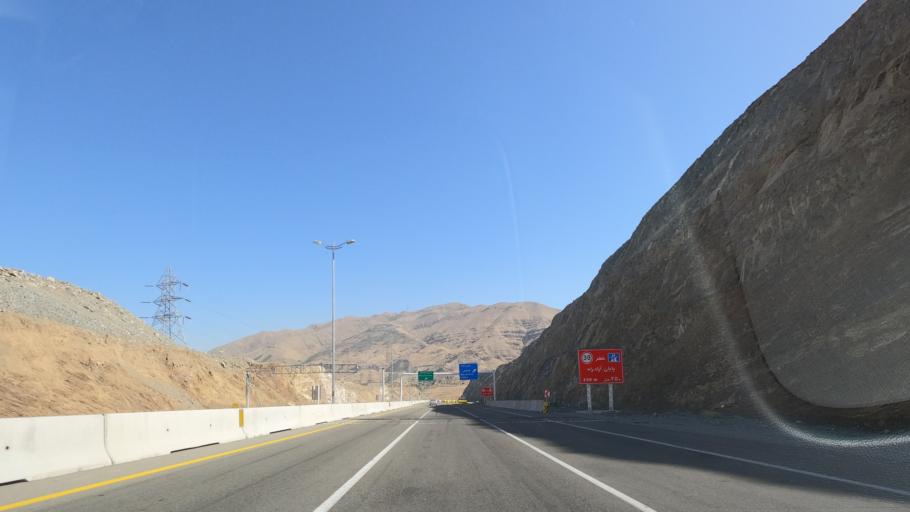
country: IR
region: Alborz
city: Karaj
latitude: 35.8182
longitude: 51.0379
